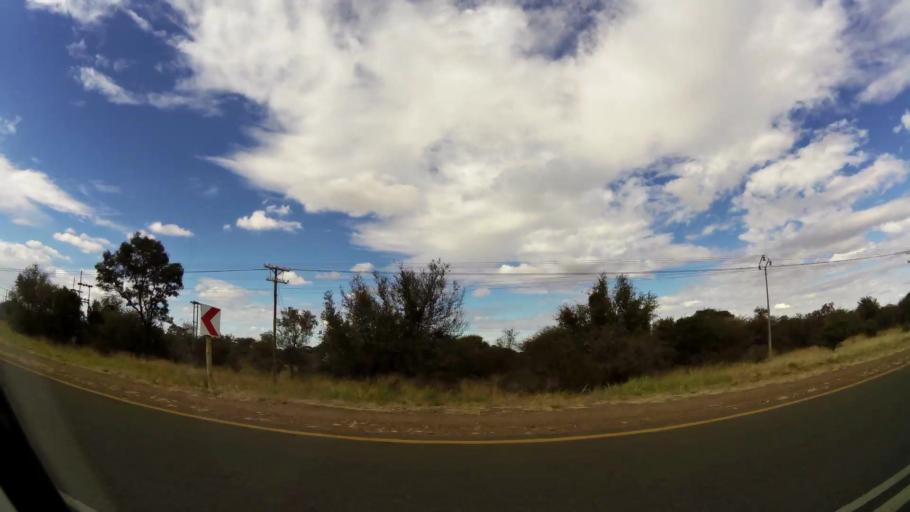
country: ZA
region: Limpopo
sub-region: Waterberg District Municipality
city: Warmbaths
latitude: -24.9012
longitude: 28.2792
